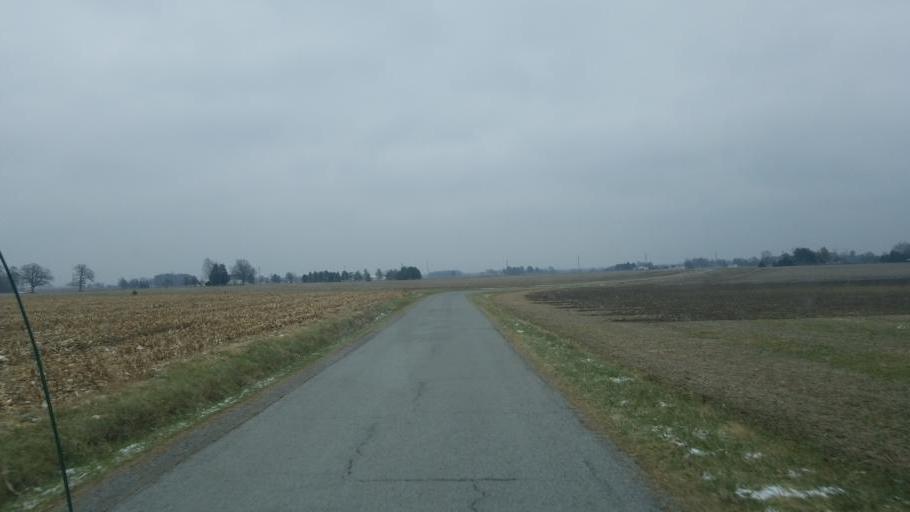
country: US
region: Ohio
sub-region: Crawford County
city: Crestline
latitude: 40.8492
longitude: -82.7363
